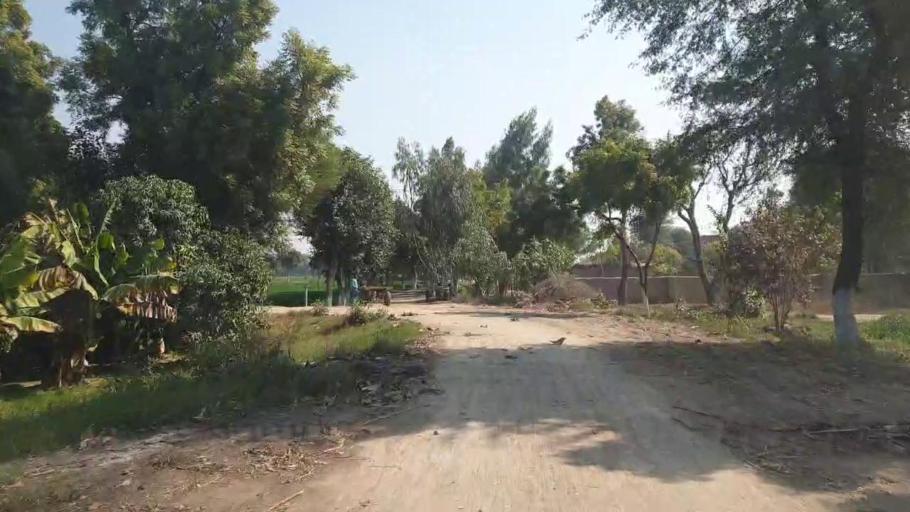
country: PK
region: Sindh
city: Tando Jam
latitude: 25.3409
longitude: 68.6136
